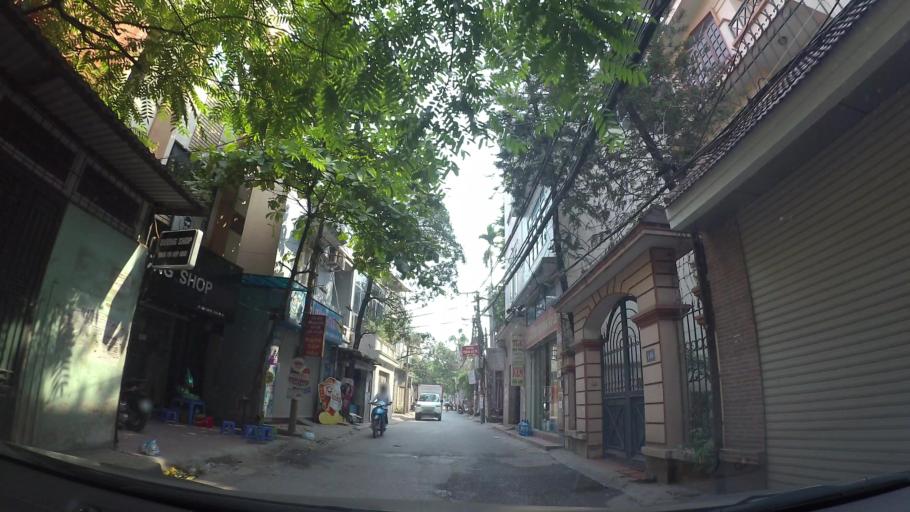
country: VN
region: Ha Noi
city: Dong Da
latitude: 20.9916
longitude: 105.8284
